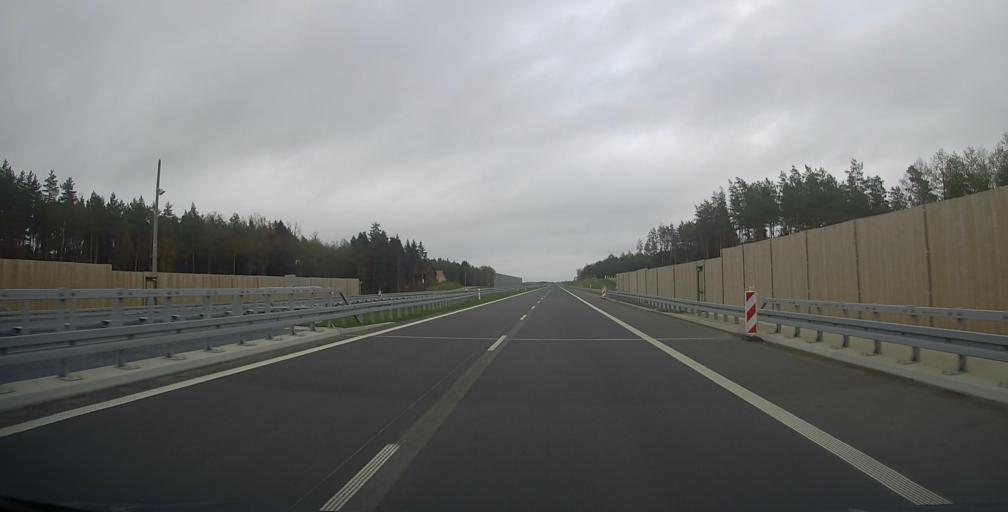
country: PL
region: Podlasie
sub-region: Powiat grajewski
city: Rajgrod
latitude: 53.8703
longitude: 22.6350
